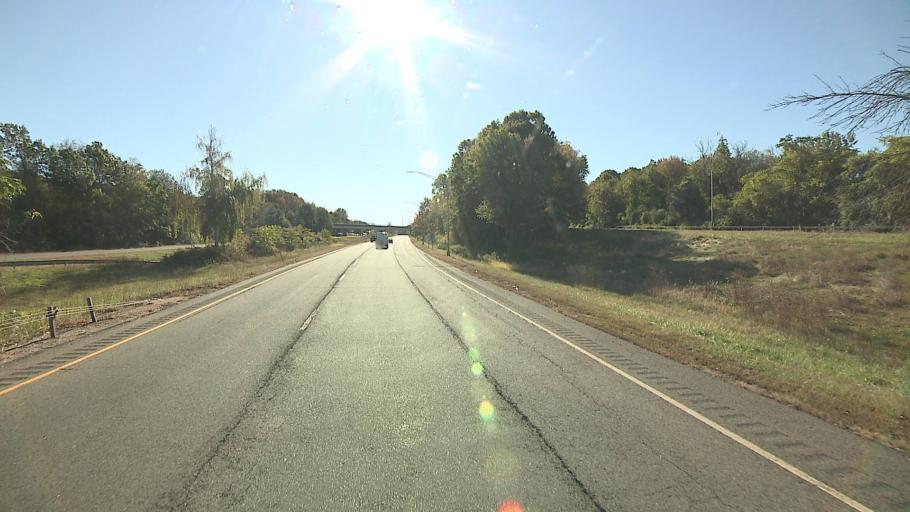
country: US
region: Connecticut
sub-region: New Haven County
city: Meriden
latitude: 41.5340
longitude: -72.7556
